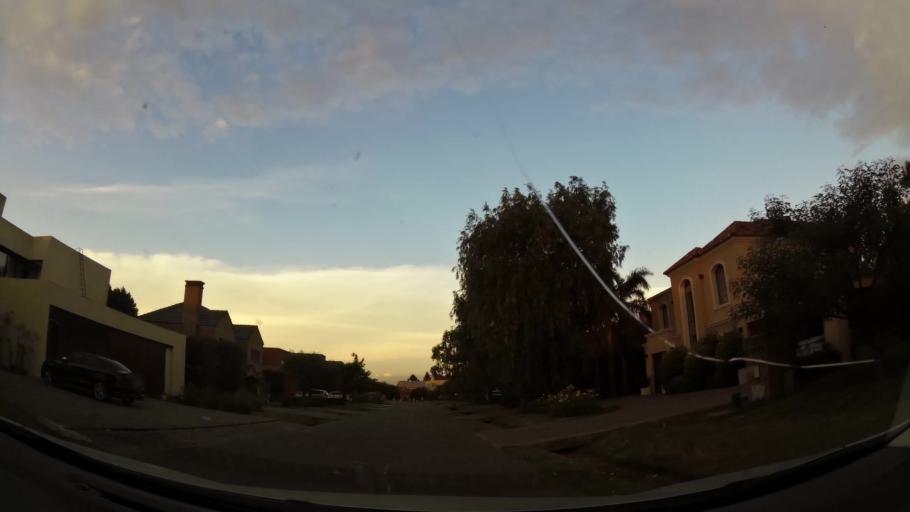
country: AR
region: Buenos Aires
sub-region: Partido de Tigre
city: Tigre
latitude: -34.4418
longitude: -58.6515
